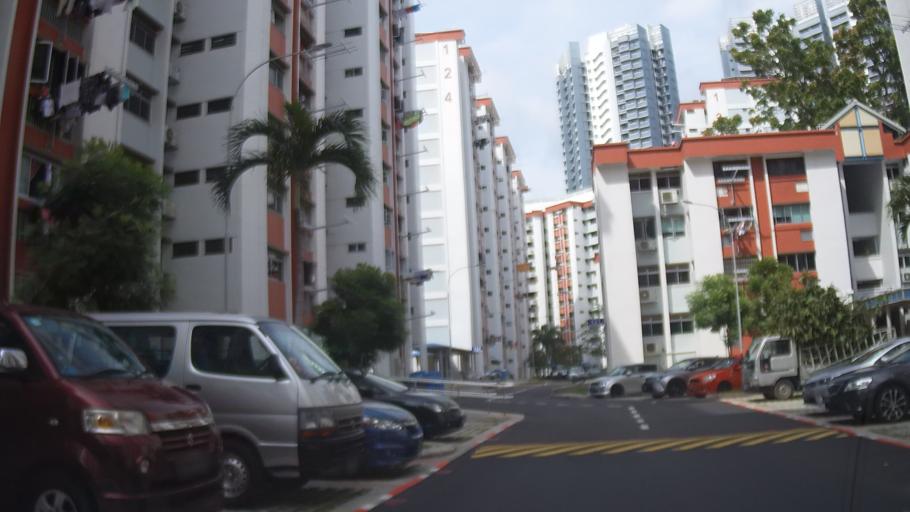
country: MY
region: Johor
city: Johor Bahru
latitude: 1.4388
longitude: 103.7807
